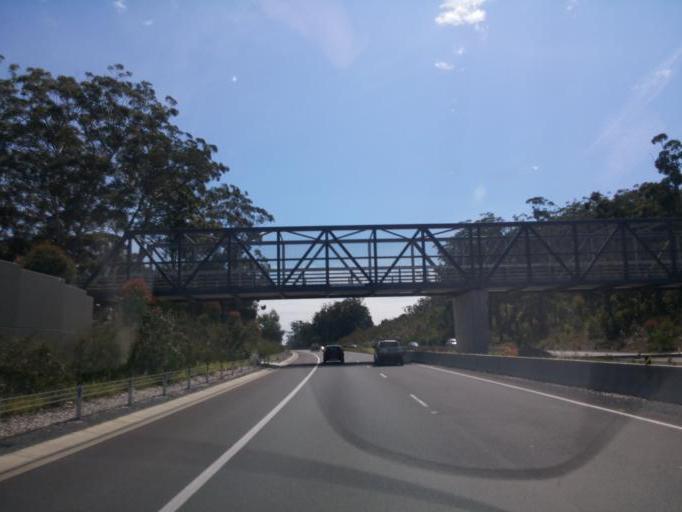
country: AU
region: New South Wales
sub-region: Great Lakes
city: Bulahdelah
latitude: -32.4147
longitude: 152.2164
